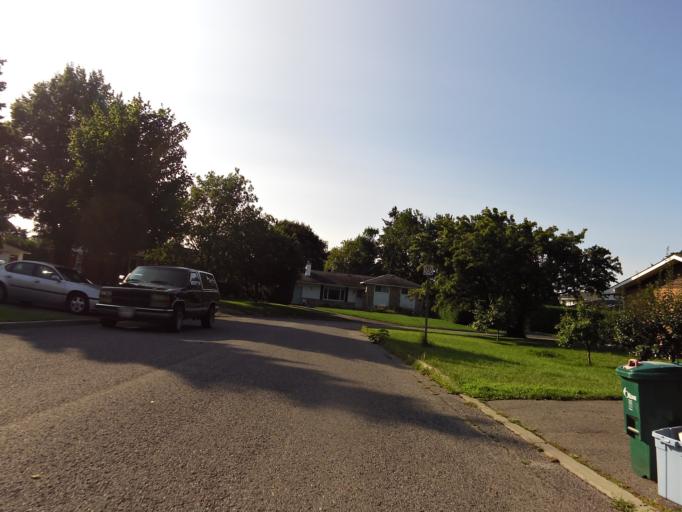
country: CA
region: Ontario
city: Ottawa
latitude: 45.3440
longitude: -75.7325
